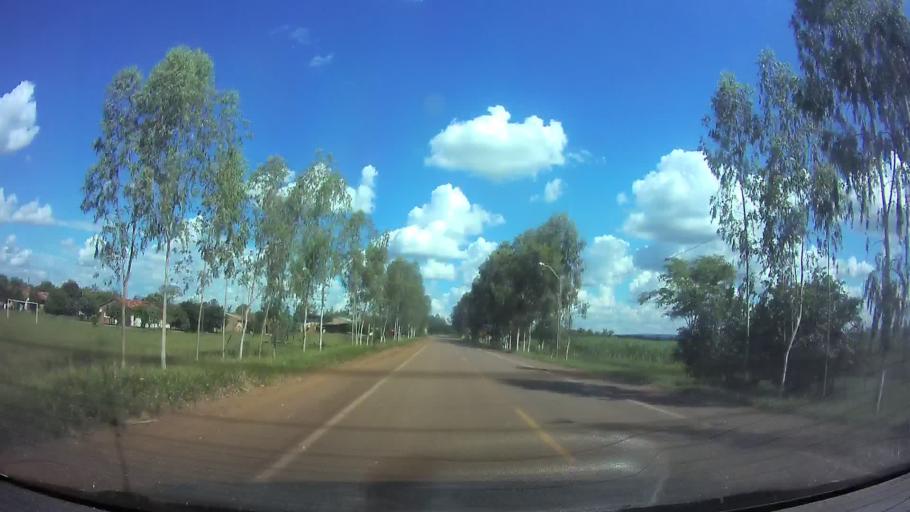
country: PY
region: Guaira
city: Coronel Martinez
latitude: -25.7834
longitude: -56.6490
